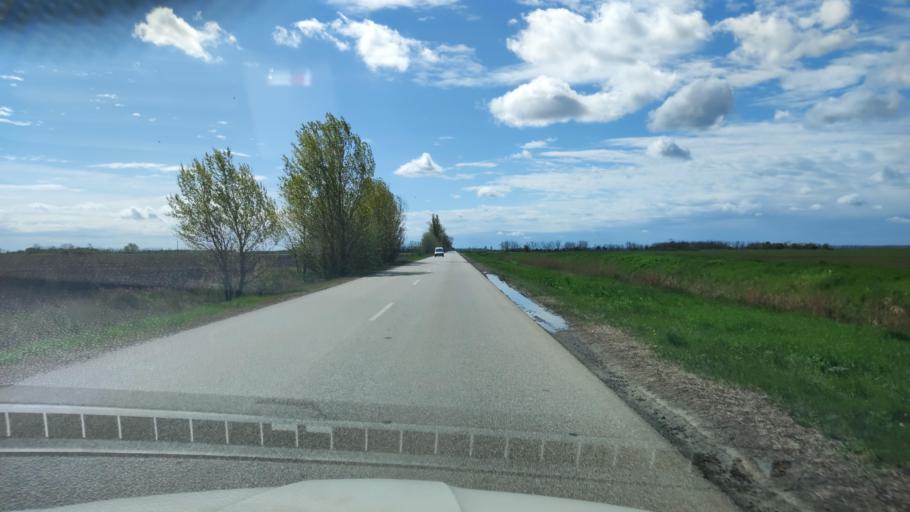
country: HU
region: Pest
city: Abony
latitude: 47.1618
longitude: 20.0052
